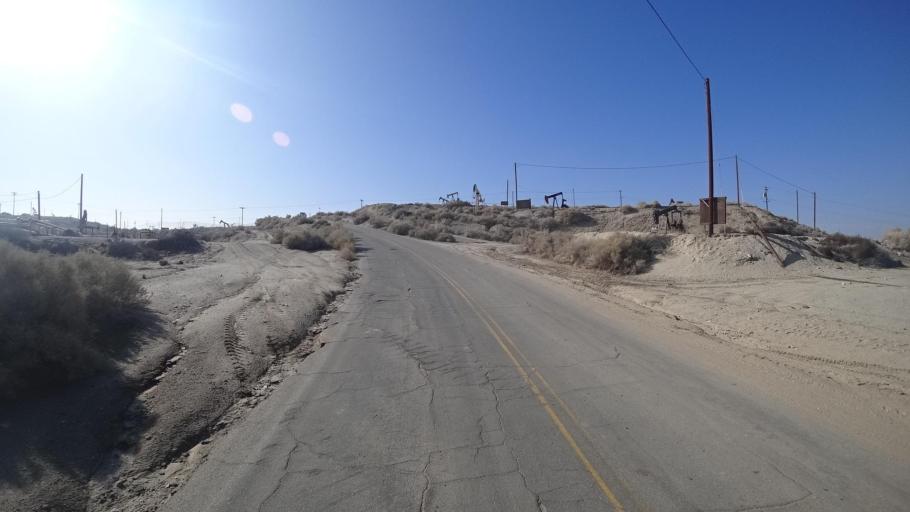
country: US
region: California
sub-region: Kern County
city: Taft Heights
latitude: 35.1206
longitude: -119.4765
